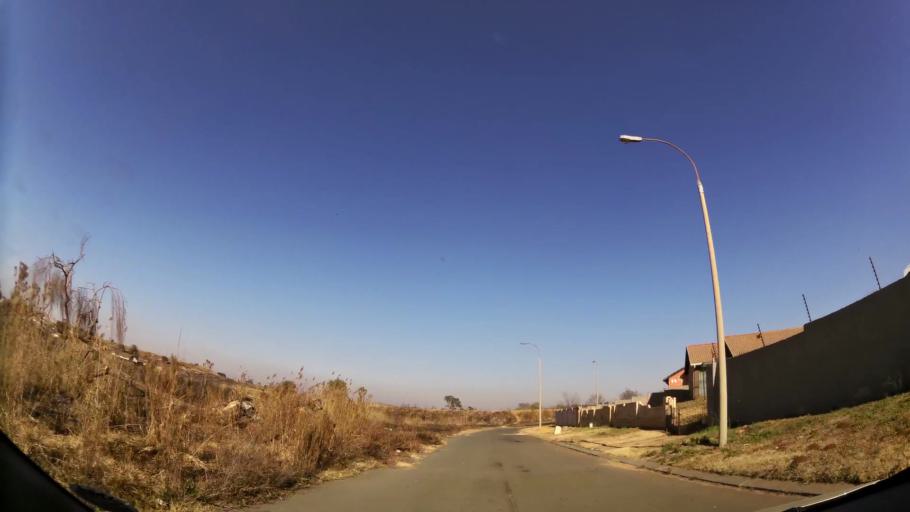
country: ZA
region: Gauteng
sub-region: City of Johannesburg Metropolitan Municipality
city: Roodepoort
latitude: -26.1541
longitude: 27.8439
